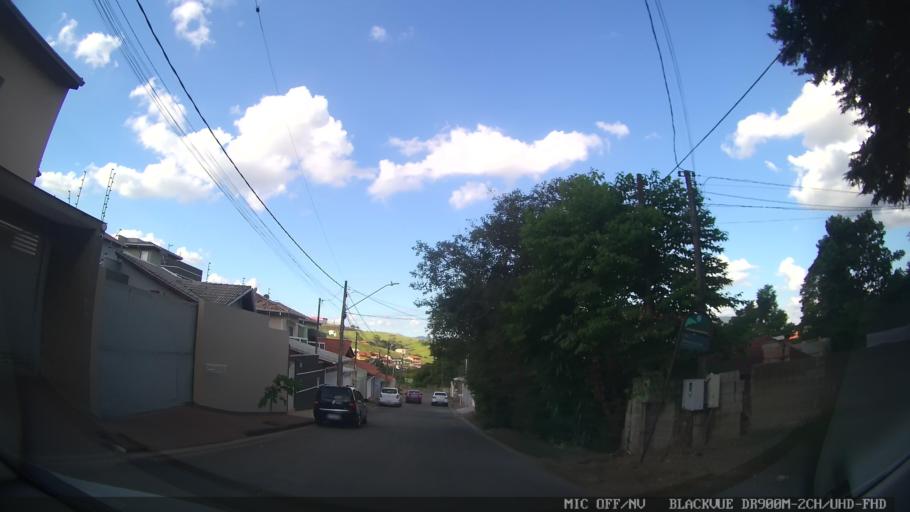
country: BR
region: Minas Gerais
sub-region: Extrema
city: Extrema
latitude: -22.8457
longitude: -46.3275
